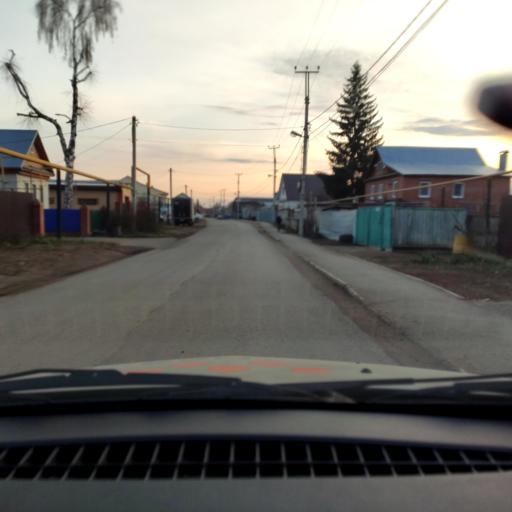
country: RU
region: Bashkortostan
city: Ufa
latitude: 54.6984
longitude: 55.9492
